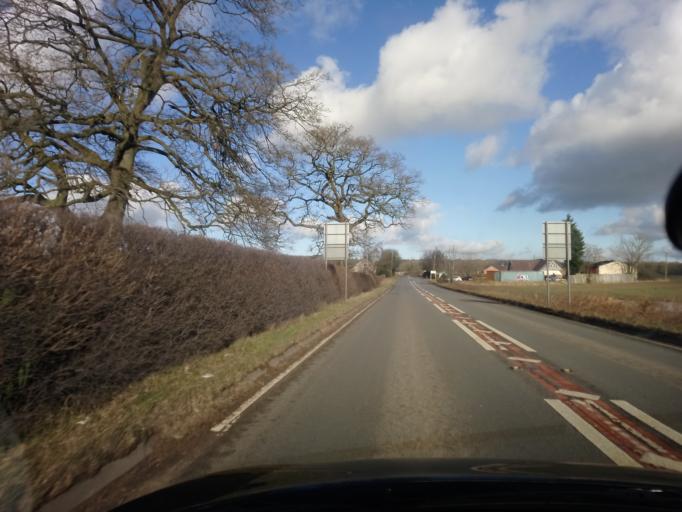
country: GB
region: England
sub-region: Shropshire
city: Clive
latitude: 52.7907
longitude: -2.7033
